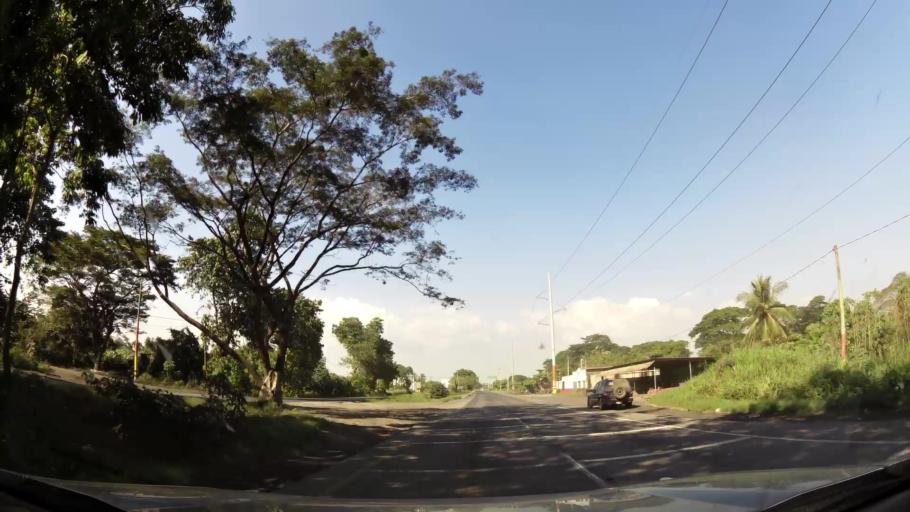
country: GT
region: Escuintla
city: Puerto San Jose
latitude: 13.9533
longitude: -90.7884
